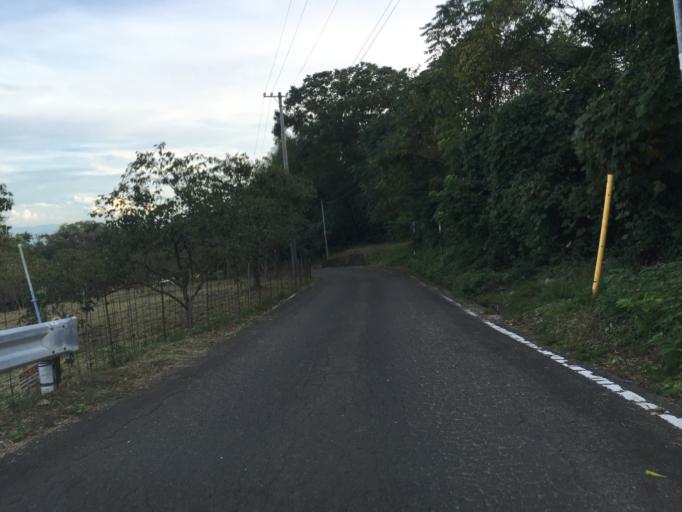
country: JP
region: Fukushima
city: Hobaramachi
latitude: 37.8854
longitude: 140.5093
